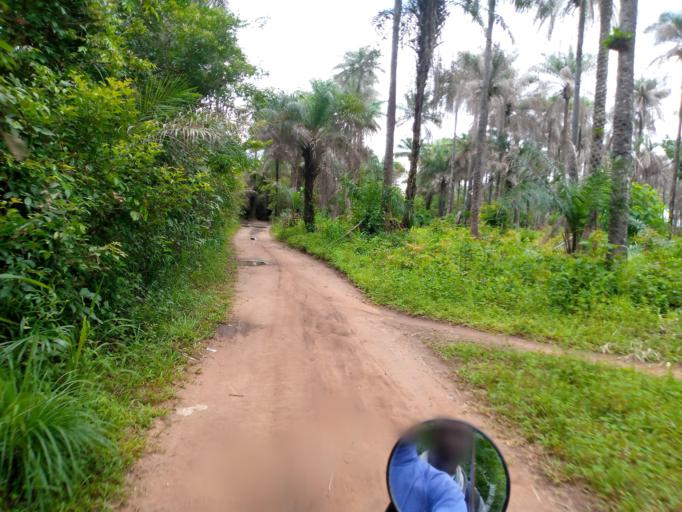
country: SL
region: Northern Province
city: Mange
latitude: 8.9781
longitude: -12.8202
